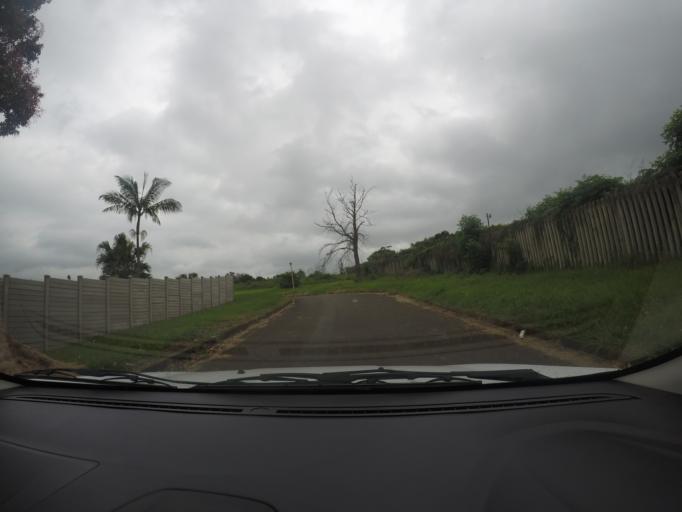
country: ZA
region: KwaZulu-Natal
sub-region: uThungulu District Municipality
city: Empangeni
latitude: -28.7442
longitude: 31.8945
